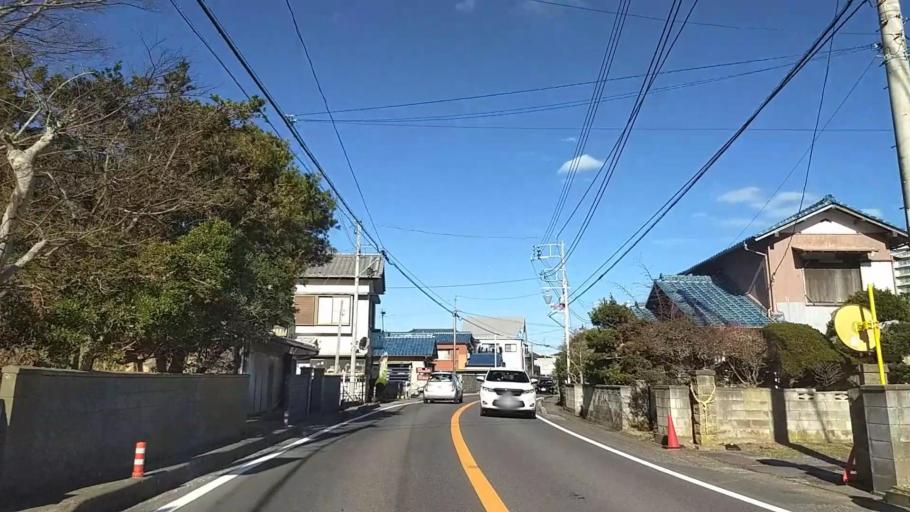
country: JP
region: Chiba
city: Katsuura
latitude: 35.1813
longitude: 140.3478
